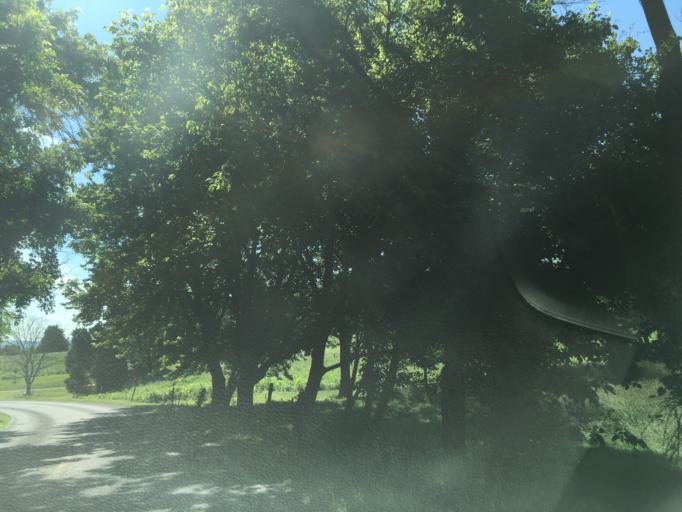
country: US
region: West Virginia
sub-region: Jefferson County
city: Bolivar
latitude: 39.3273
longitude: -77.6941
